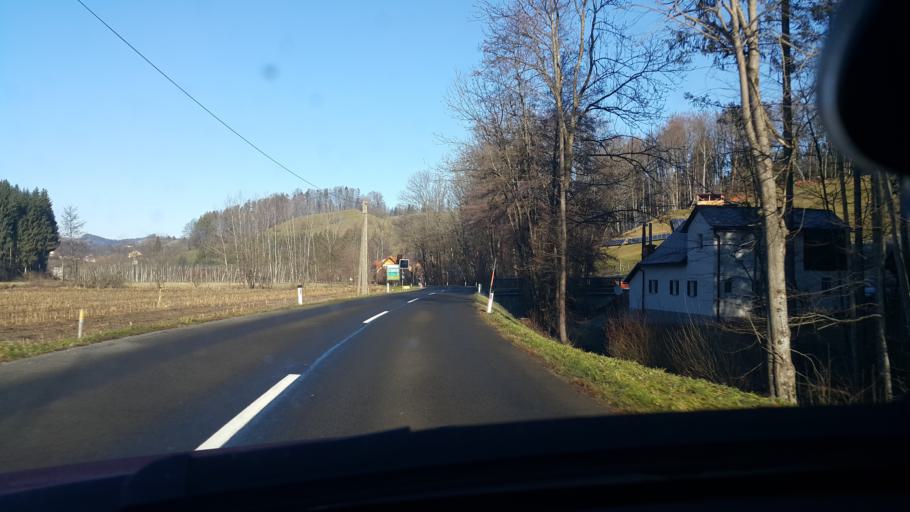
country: AT
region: Styria
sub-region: Politischer Bezirk Leibnitz
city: Leutschach
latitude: 46.6537
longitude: 15.4864
